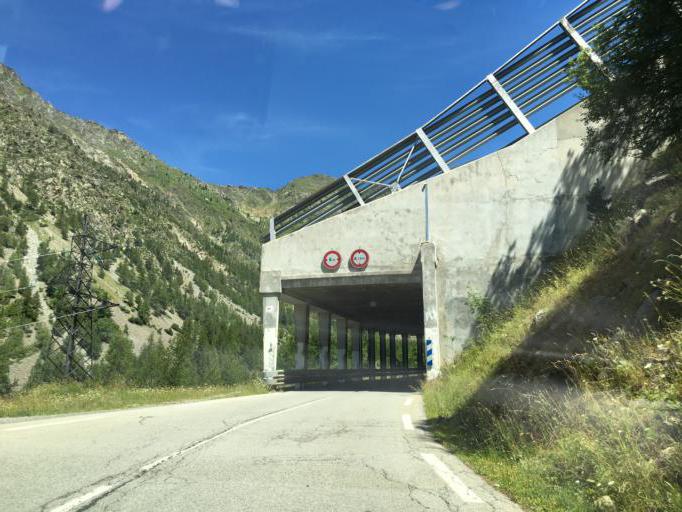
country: IT
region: Piedmont
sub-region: Provincia di Cuneo
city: Sambuco
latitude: 44.2017
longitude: 7.0916
